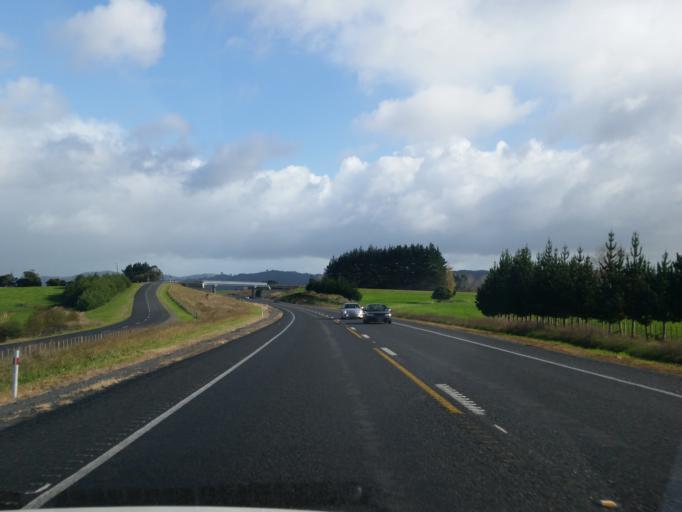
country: NZ
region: Waikato
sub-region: Waikato District
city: Te Kauwhata
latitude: -37.2222
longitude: 175.1426
